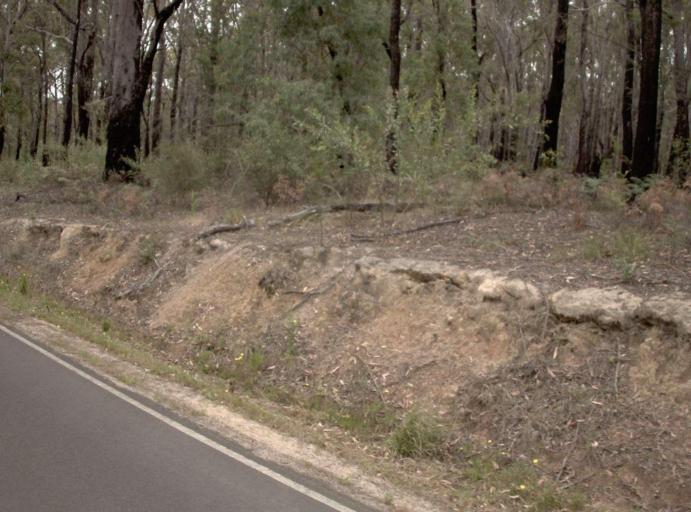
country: AU
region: Victoria
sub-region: Latrobe
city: Traralgon
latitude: -38.4755
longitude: 146.8221
